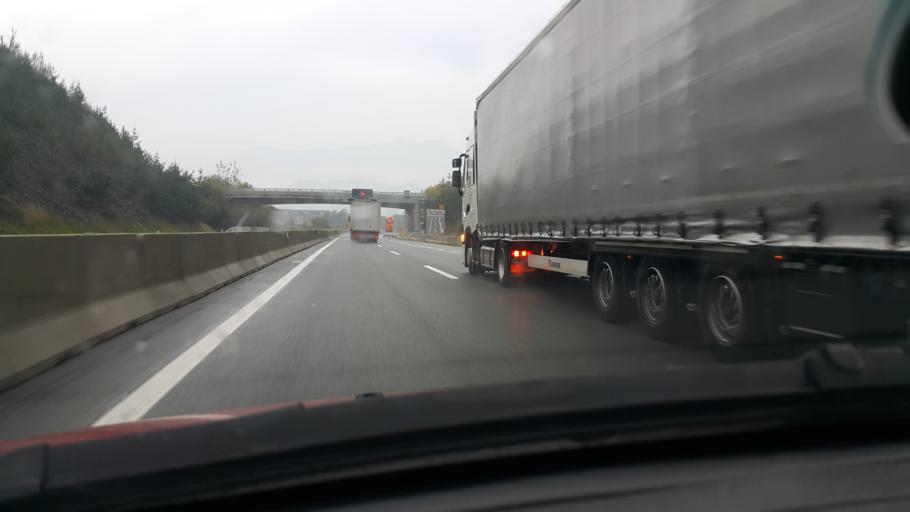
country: AT
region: Carinthia
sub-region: Politischer Bezirk Volkermarkt
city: Voelkermarkt
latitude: 46.6507
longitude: 14.5620
